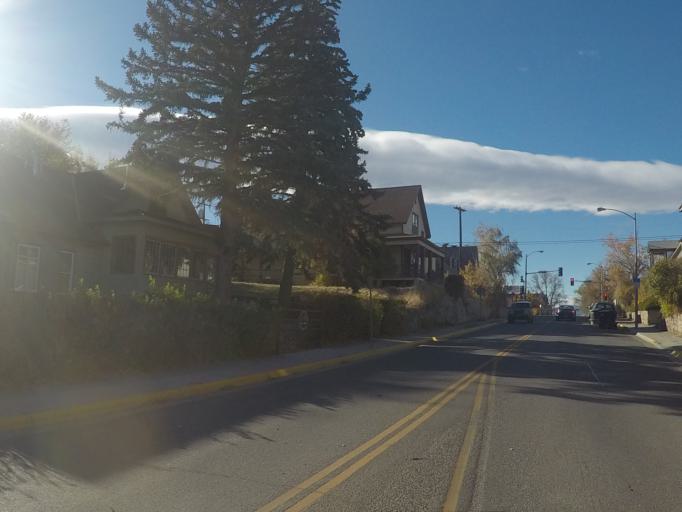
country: US
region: Montana
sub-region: Lewis and Clark County
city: Helena
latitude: 46.5866
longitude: -112.0325
